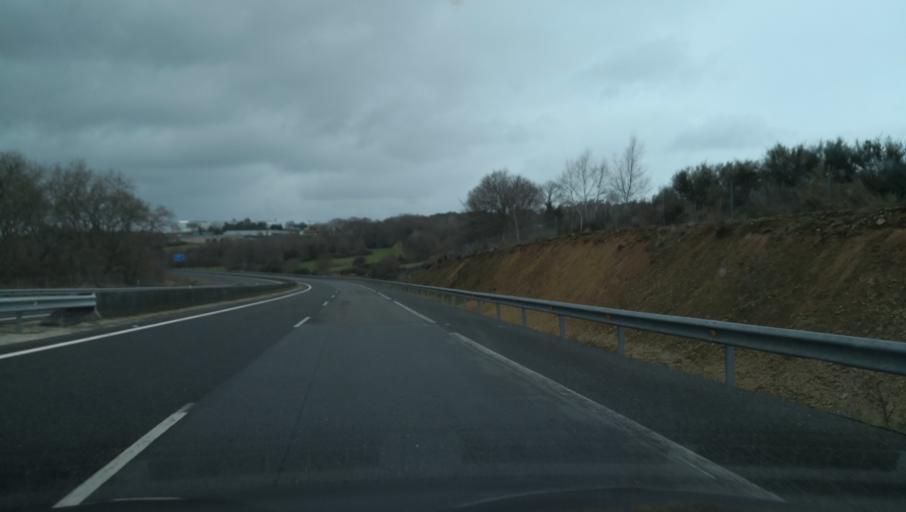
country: ES
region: Galicia
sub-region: Provincia de Pontevedra
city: Lalin
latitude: 42.6655
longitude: -8.1472
